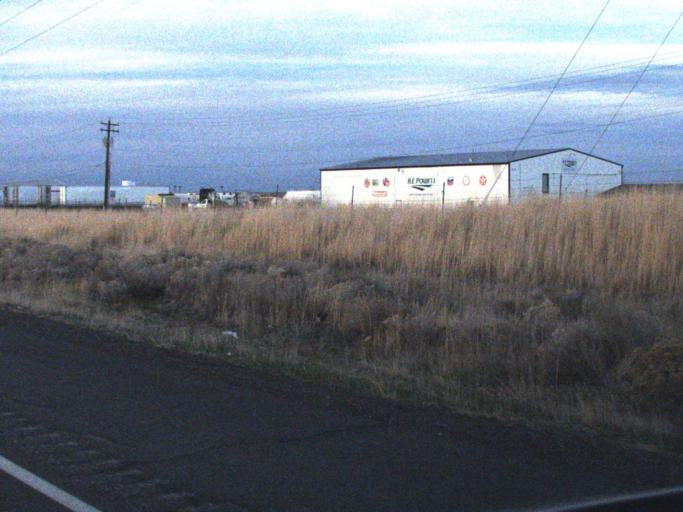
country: US
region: Washington
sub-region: Walla Walla County
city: Burbank
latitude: 46.2341
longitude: -119.0489
